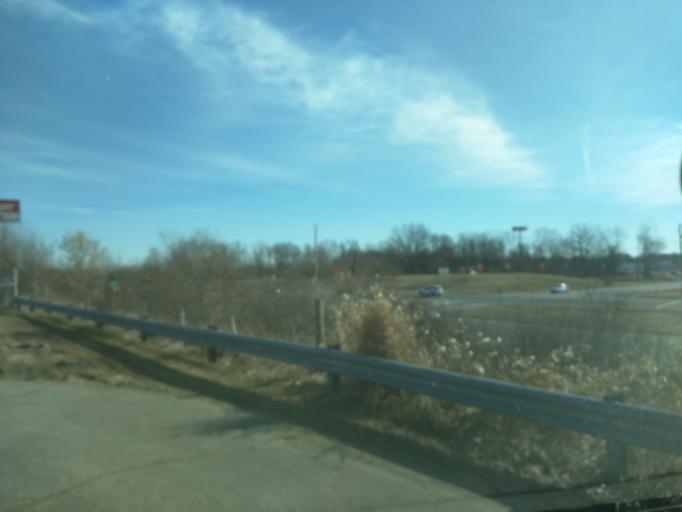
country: US
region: Michigan
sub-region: Ingham County
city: Haslett
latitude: 42.7753
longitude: -84.4115
